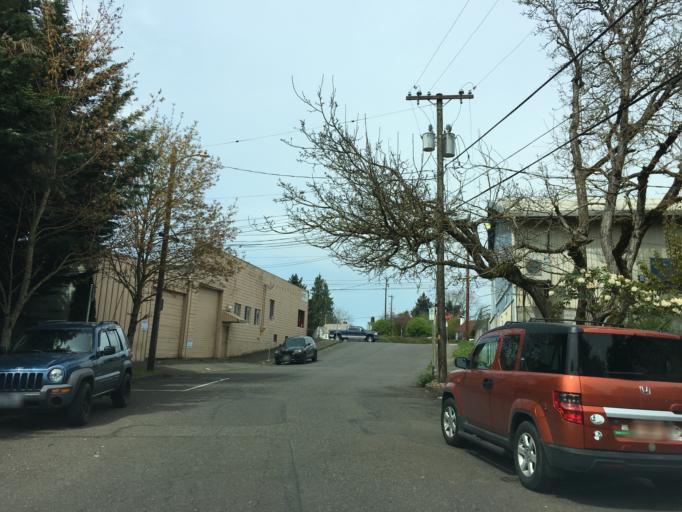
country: US
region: Oregon
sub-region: Multnomah County
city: Lents
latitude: 45.5546
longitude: -122.5716
